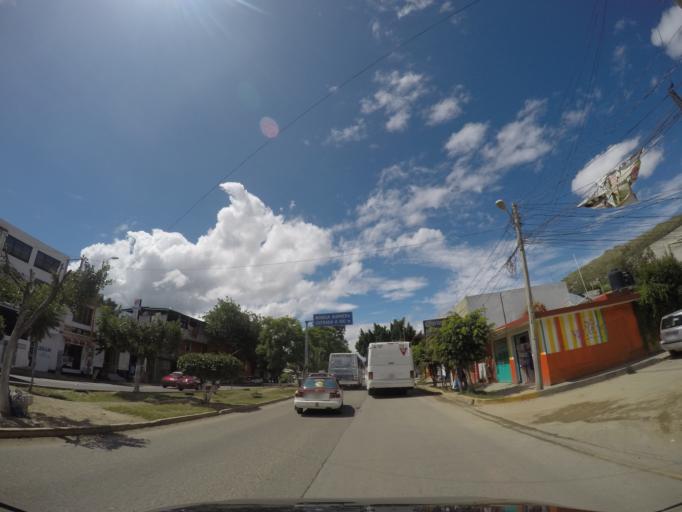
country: MX
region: Oaxaca
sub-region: Santa Cruz Xoxocotlan
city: Santa Cruz Xoxocotlan
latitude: 17.0472
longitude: -96.7312
